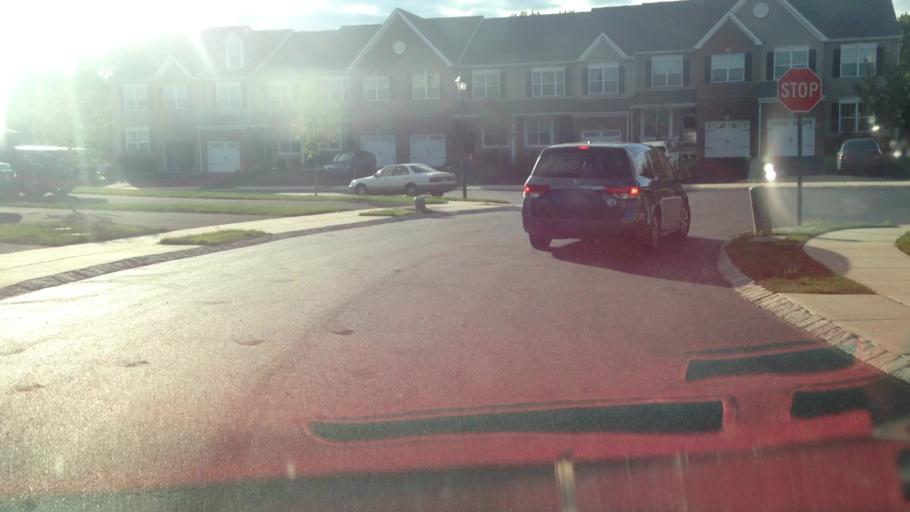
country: US
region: Pennsylvania
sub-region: Bucks County
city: Penndel
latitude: 40.1336
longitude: -74.9371
